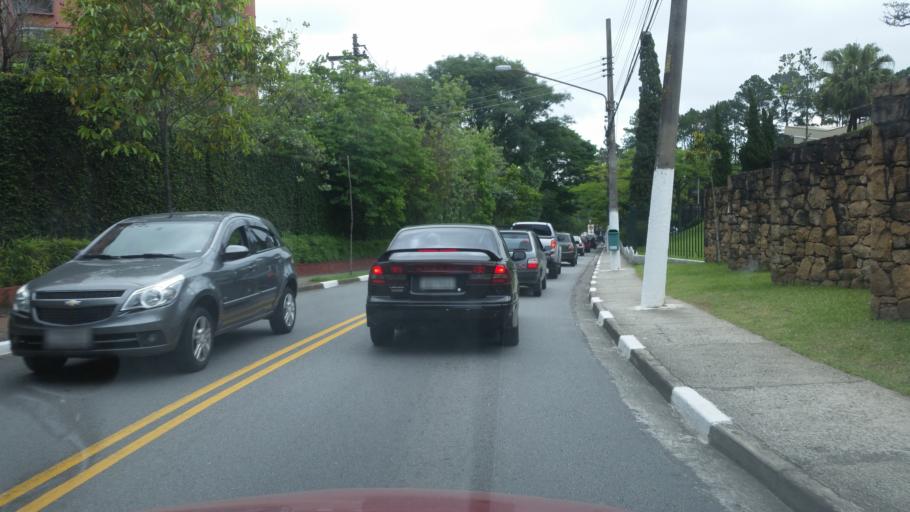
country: BR
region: Sao Paulo
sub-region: Diadema
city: Diadema
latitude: -23.6589
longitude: -46.6843
